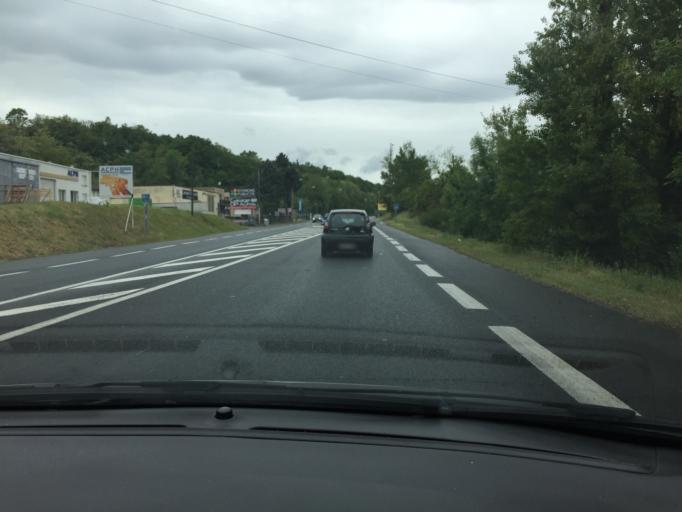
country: FR
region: Rhone-Alpes
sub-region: Departement du Rhone
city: Montagny
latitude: 45.6233
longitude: 4.7638
